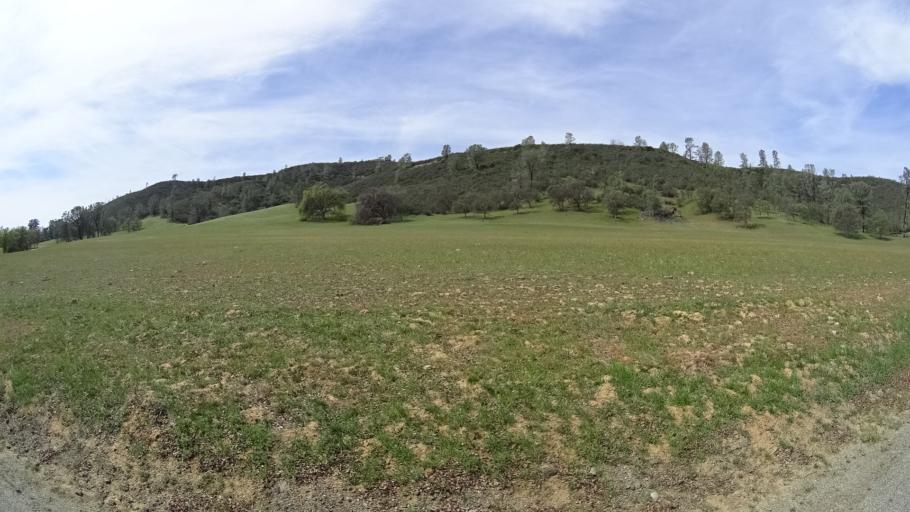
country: US
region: California
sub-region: Glenn County
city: Willows
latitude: 39.6045
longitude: -122.5263
